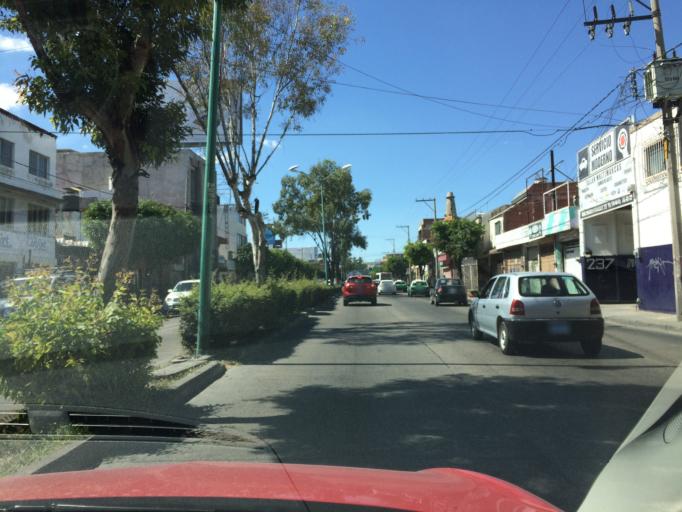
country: MX
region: Guanajuato
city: Leon
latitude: 21.1148
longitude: -101.6822
